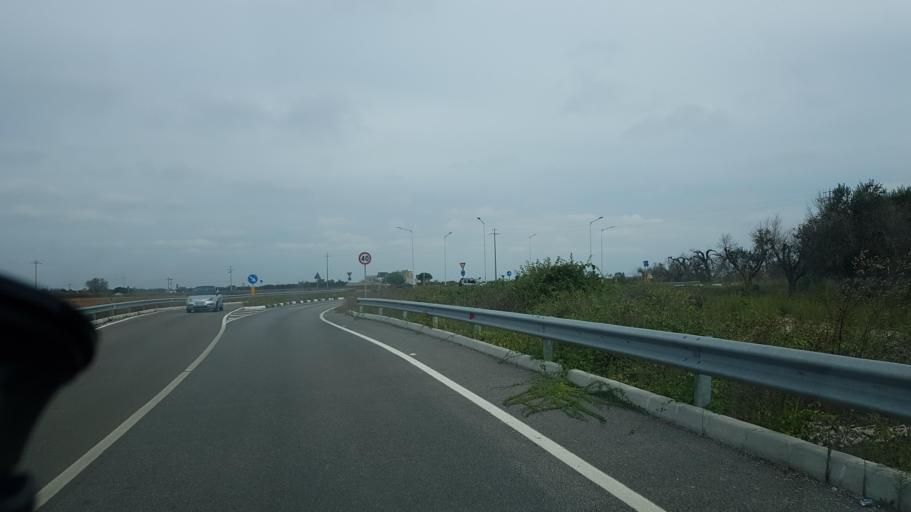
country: IT
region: Apulia
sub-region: Provincia di Lecce
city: Guagnano
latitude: 40.4207
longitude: 17.9499
